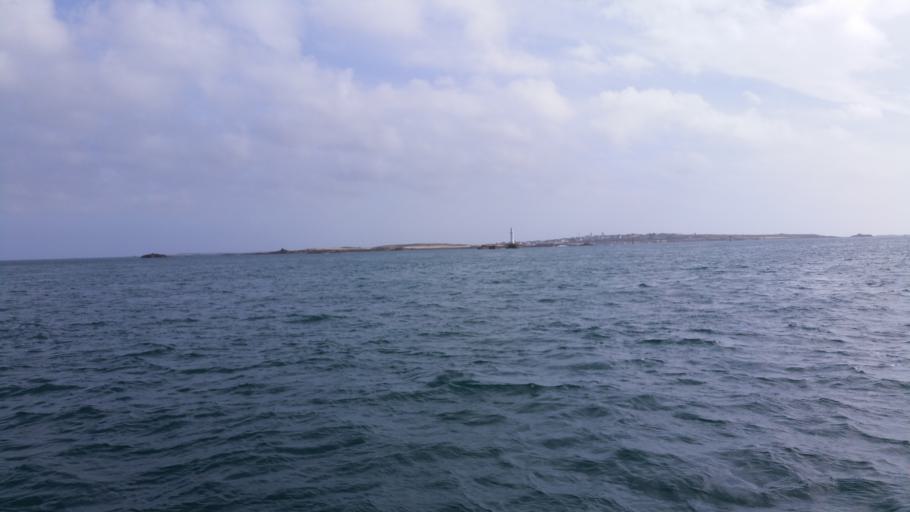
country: FR
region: Brittany
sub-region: Departement du Finistere
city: Le Conquet
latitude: 48.4175
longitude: -4.9446
